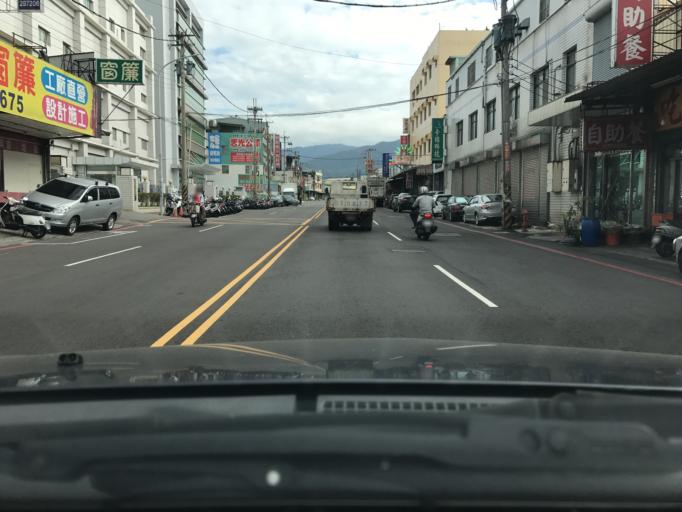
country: TW
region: Taiwan
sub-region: Hsinchu
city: Zhubei
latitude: 24.7339
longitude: 121.0984
